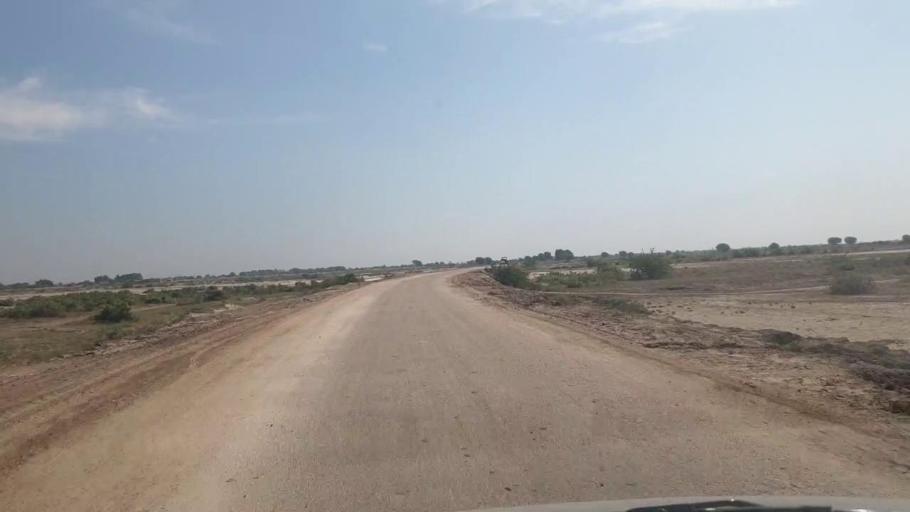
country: PK
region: Sindh
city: Digri
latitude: 24.9749
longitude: 69.1212
